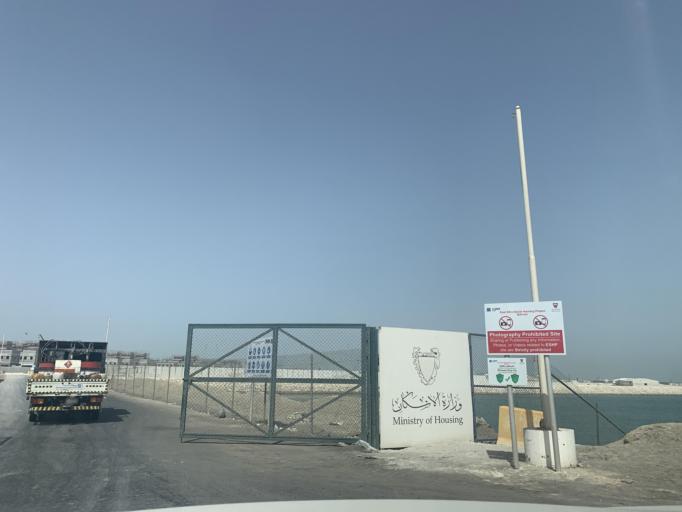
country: BH
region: Northern
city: Sitrah
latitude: 26.1562
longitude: 50.6304
